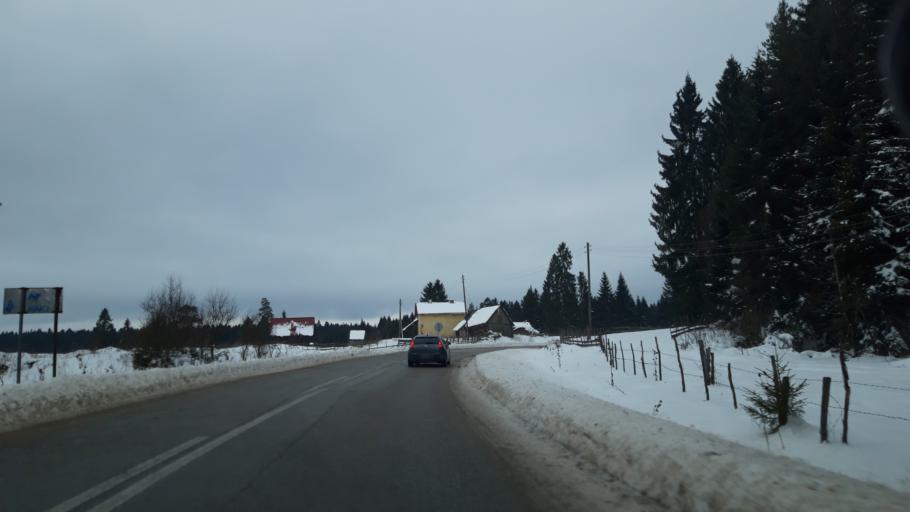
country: BA
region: Republika Srpska
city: Han Pijesak
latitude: 44.0254
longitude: 18.8982
